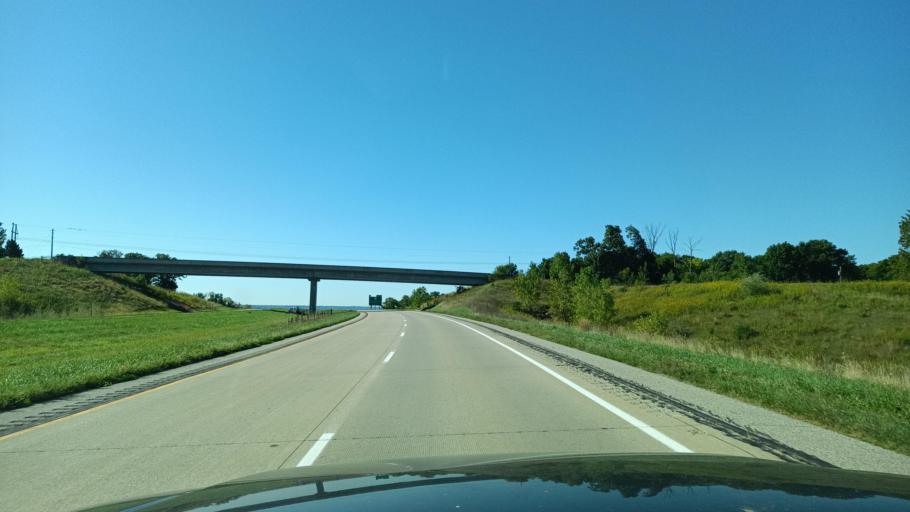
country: US
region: Iowa
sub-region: Lee County
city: Fort Madison
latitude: 40.6402
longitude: -91.3791
